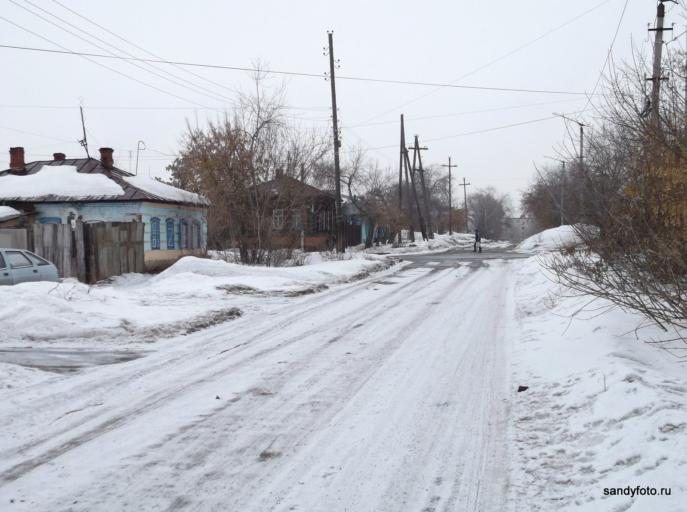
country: RU
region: Chelyabinsk
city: Troitsk
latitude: 54.0890
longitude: 61.5517
